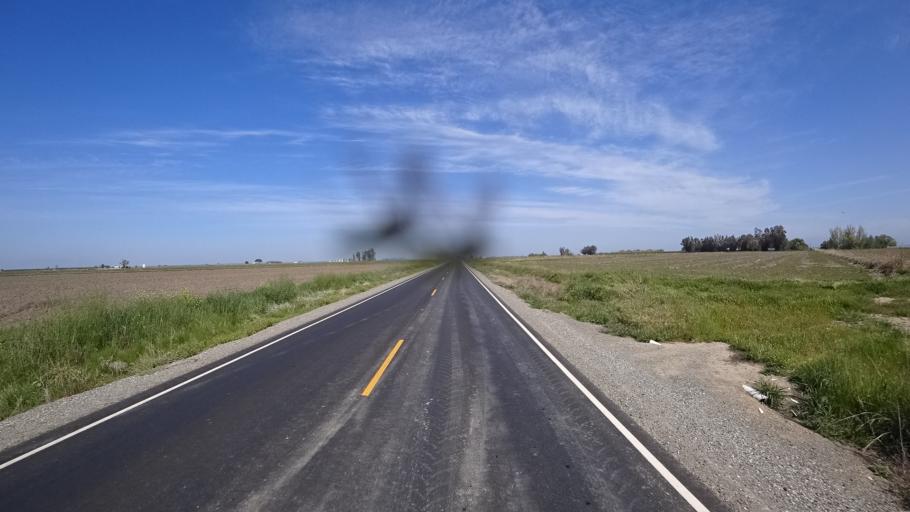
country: US
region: California
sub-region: Glenn County
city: Willows
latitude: 39.5912
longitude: -122.0649
